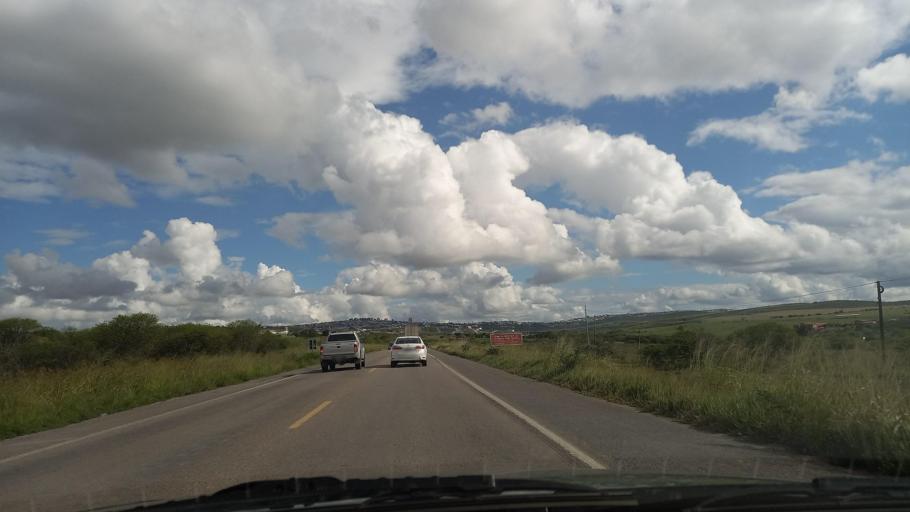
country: BR
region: Pernambuco
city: Garanhuns
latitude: -8.8362
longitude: -36.4554
